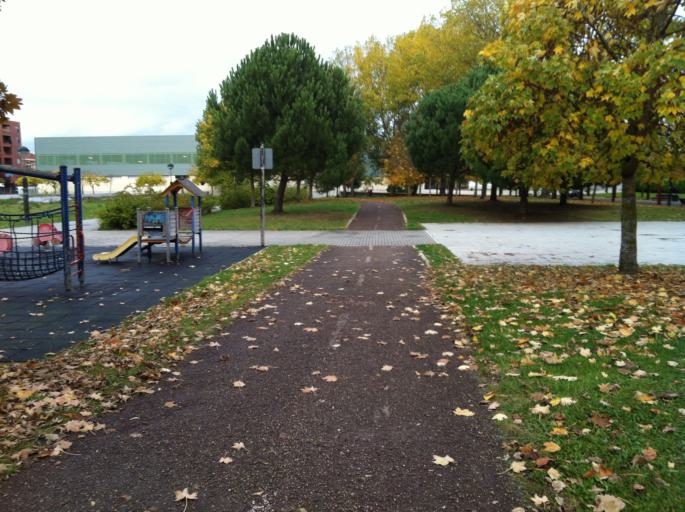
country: ES
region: Basque Country
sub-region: Provincia de Alava
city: Gasteiz / Vitoria
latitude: 42.8641
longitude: -2.6889
